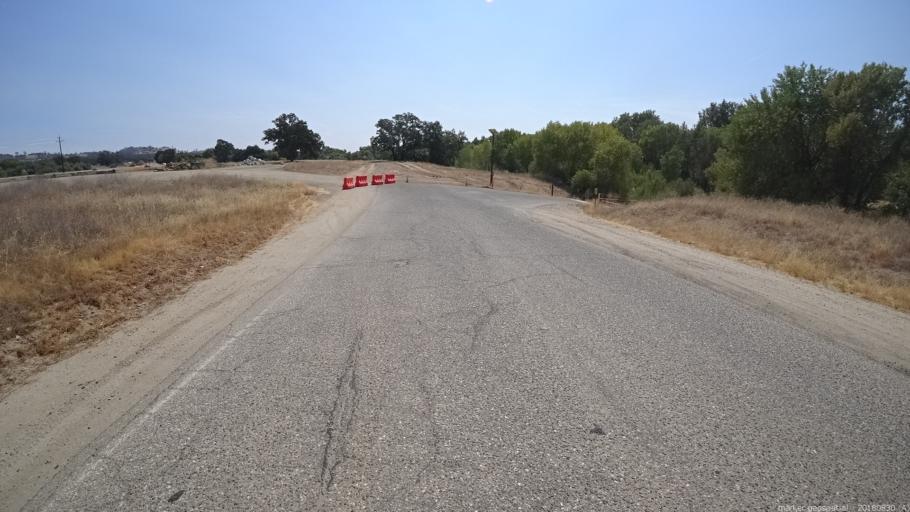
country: US
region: California
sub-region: Monterey County
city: King City
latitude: 35.9848
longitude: -121.2384
